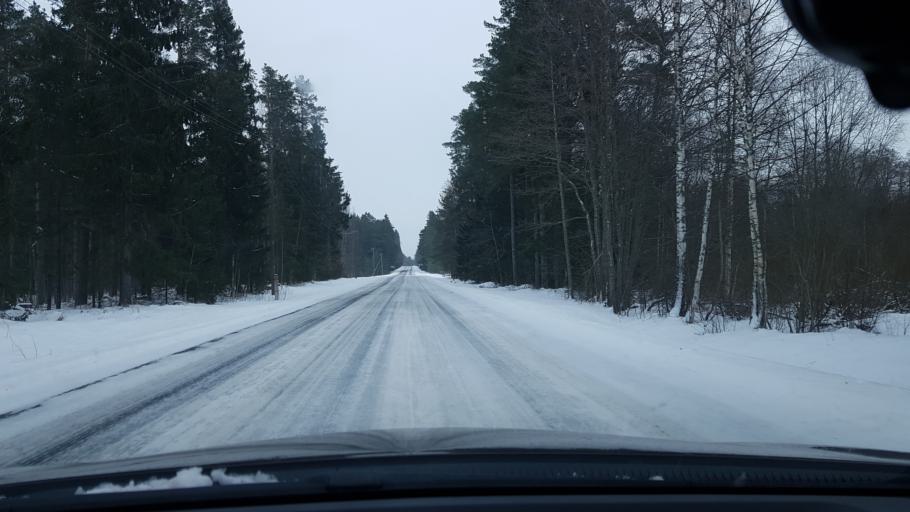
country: EE
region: Harju
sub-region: Loksa linn
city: Loksa
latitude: 59.5583
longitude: 25.8320
